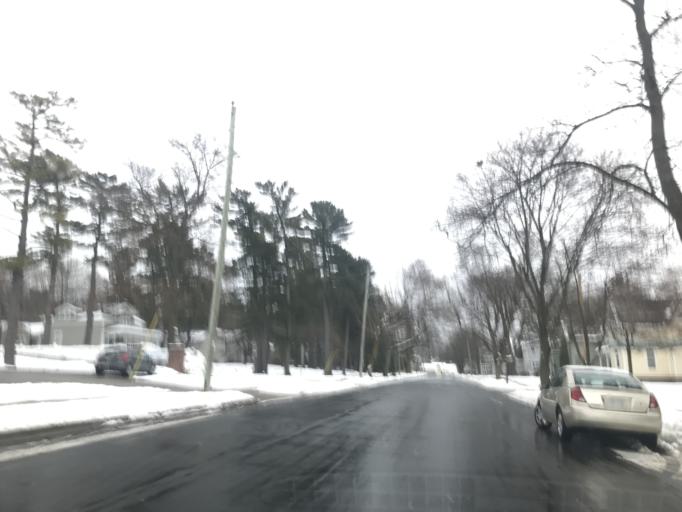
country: US
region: Wisconsin
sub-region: Door County
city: Sturgeon Bay
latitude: 44.8385
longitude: -87.3734
